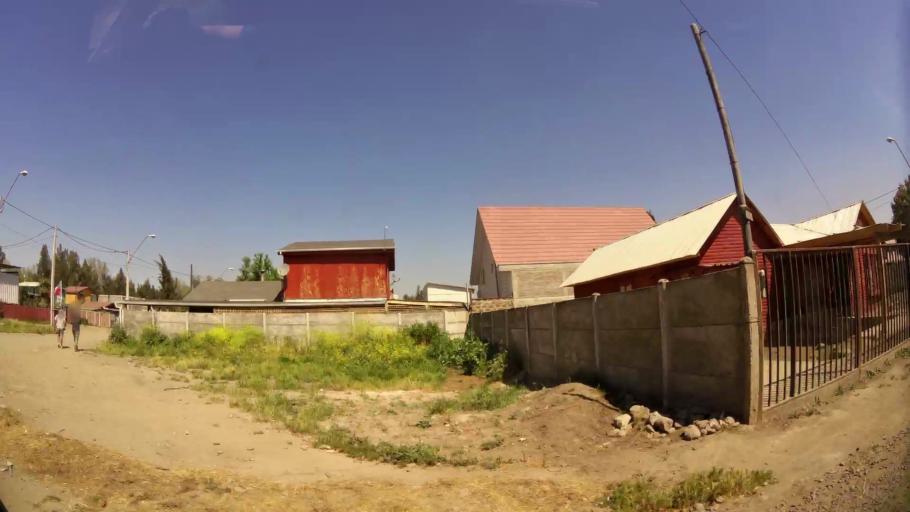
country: CL
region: Santiago Metropolitan
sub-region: Provincia de Talagante
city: Penaflor
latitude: -33.5845
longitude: -70.8056
